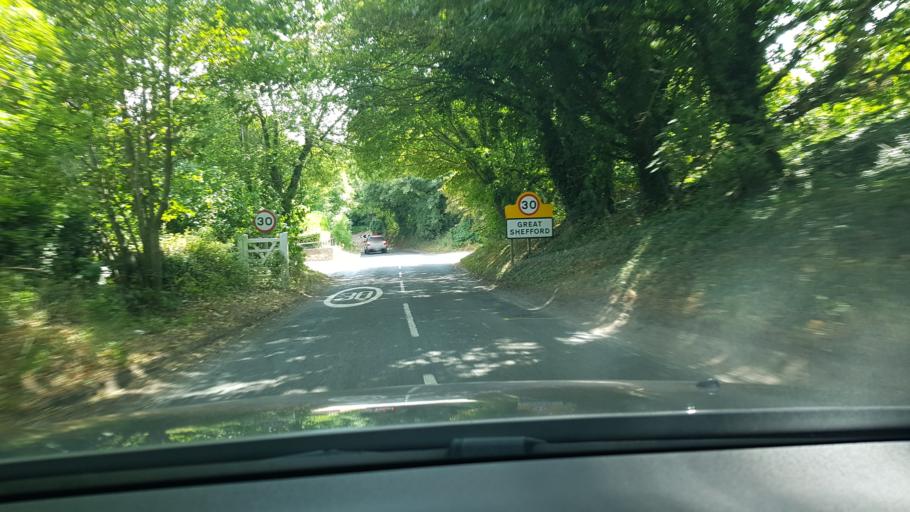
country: GB
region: England
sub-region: West Berkshire
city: Wickham
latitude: 51.4754
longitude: -1.4555
